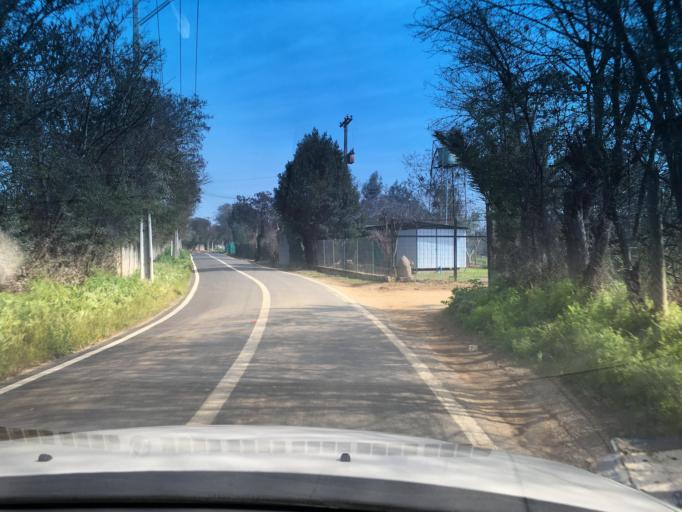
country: CL
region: Valparaiso
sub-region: Provincia de Marga Marga
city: Limache
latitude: -33.0125
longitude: -71.2077
